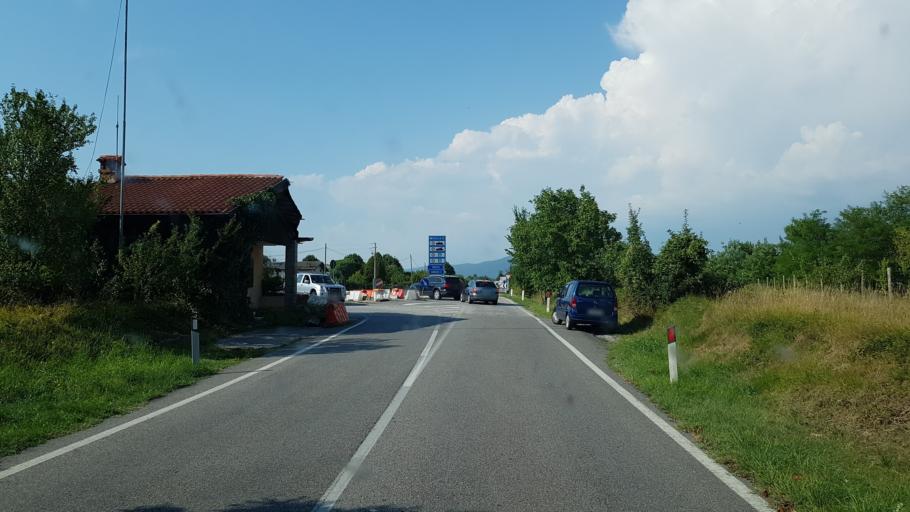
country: SI
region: Miren-Kostanjevica
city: Miren
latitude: 45.8994
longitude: 13.6089
